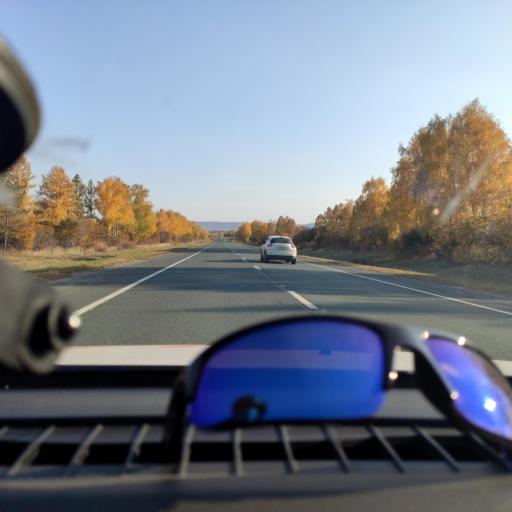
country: RU
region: Samara
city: Volzhskiy
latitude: 53.4724
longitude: 50.1213
